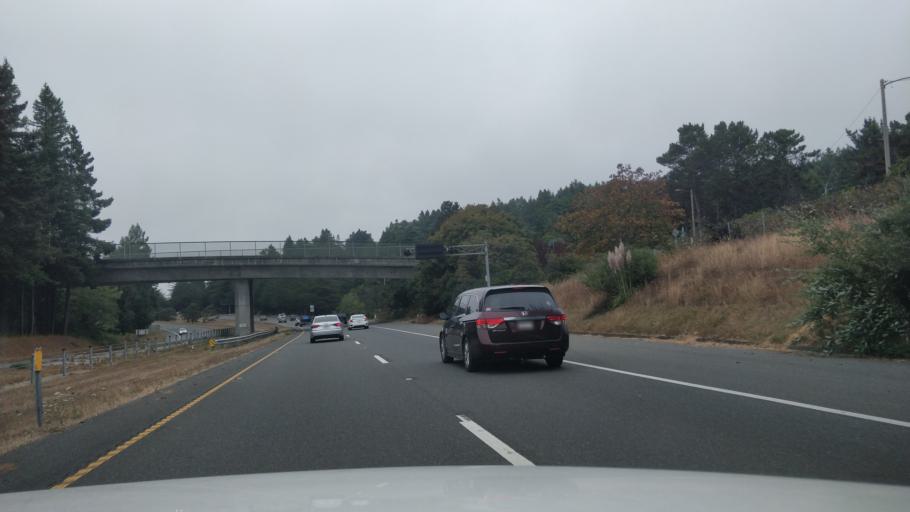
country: US
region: California
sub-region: Humboldt County
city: Arcata
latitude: 40.8852
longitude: -124.0801
